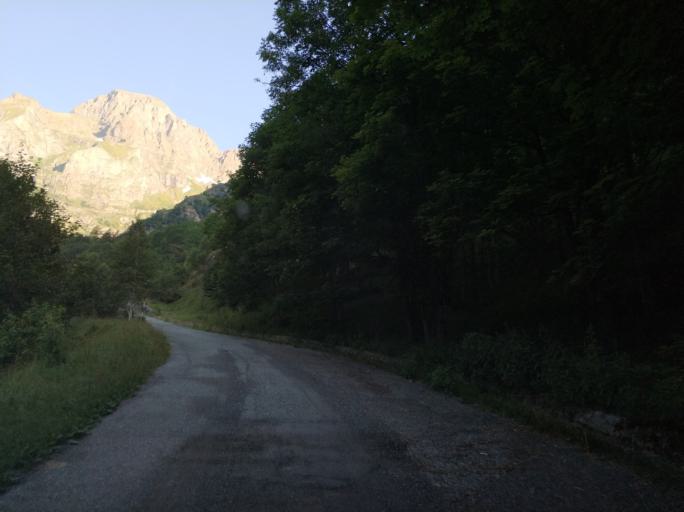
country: IT
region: Piedmont
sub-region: Provincia di Torino
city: Usseglio
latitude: 45.2380
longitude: 7.1991
